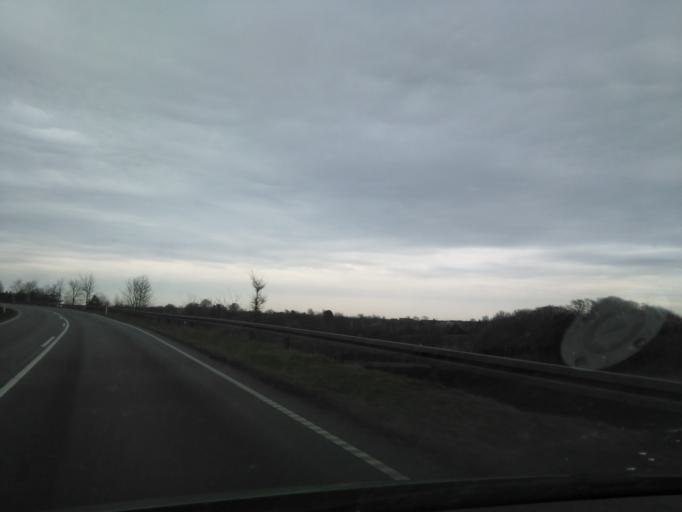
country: DK
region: North Denmark
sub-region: Mariagerfjord Kommune
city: Hobro
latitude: 56.6704
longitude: 9.8434
